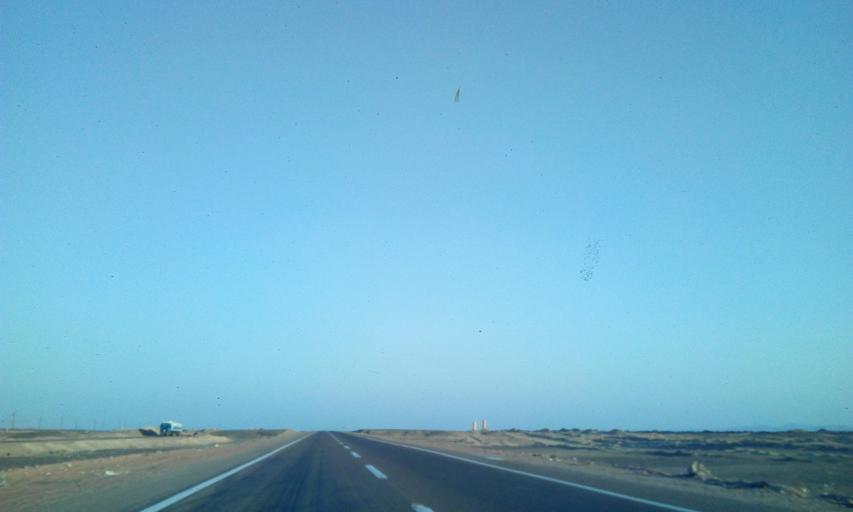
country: EG
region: South Sinai
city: Tor
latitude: 28.0428
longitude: 33.2862
